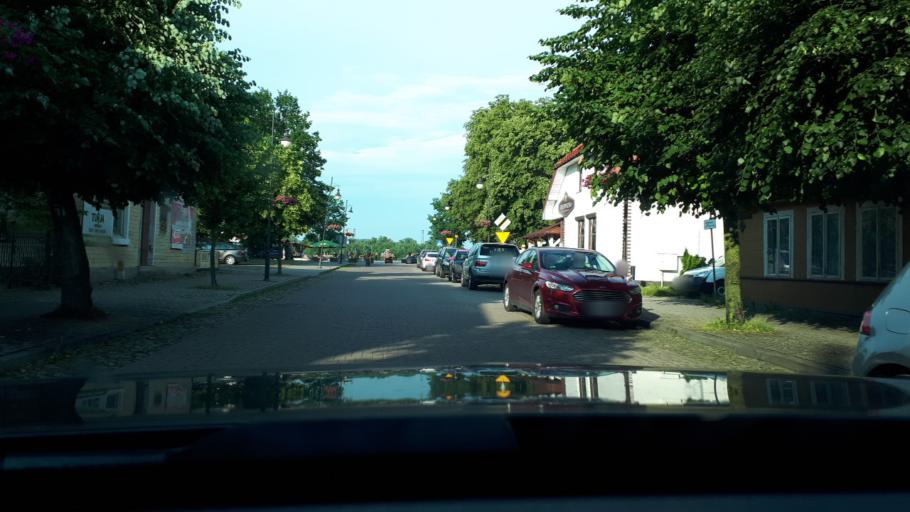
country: PL
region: Podlasie
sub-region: Powiat bialostocki
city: Suprasl
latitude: 53.2063
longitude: 23.3420
